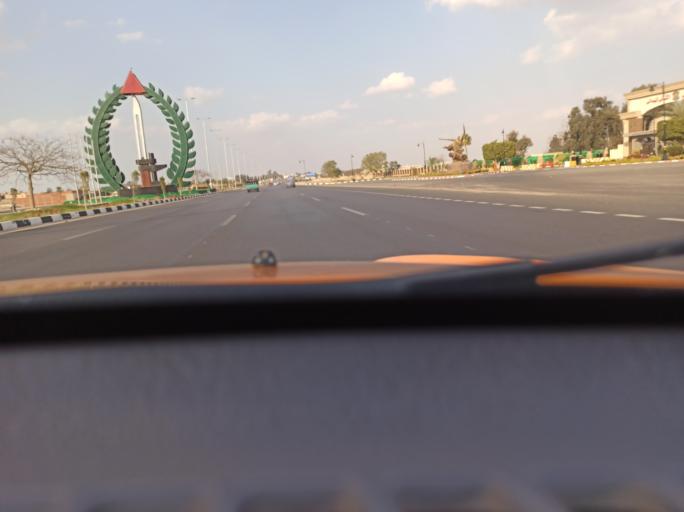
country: EG
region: Al Isma'iliyah
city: Ismailia
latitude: 30.6069
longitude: 32.2143
